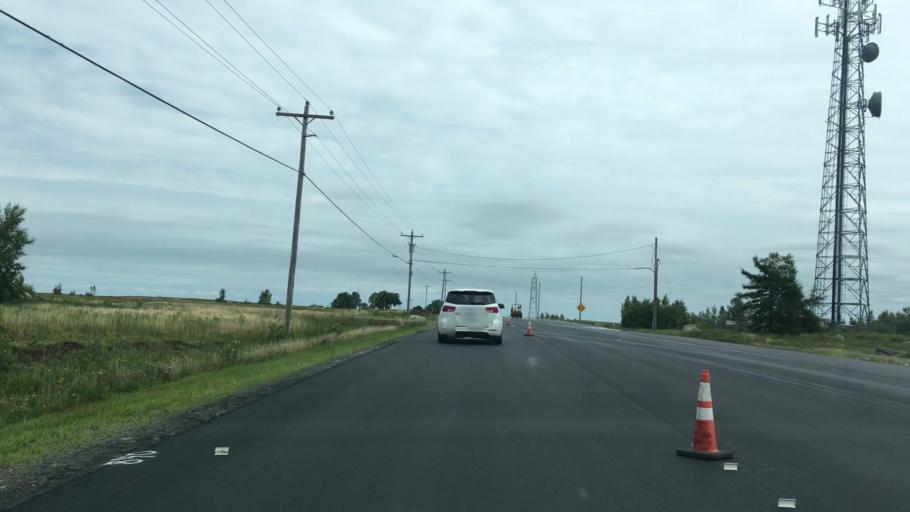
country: US
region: Maine
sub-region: Washington County
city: Machias
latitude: 44.9650
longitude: -67.6505
